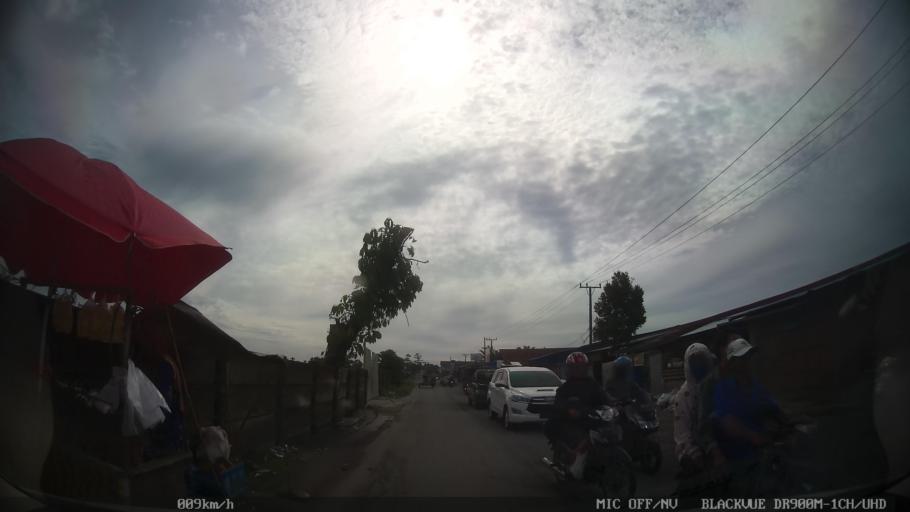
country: ID
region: North Sumatra
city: Medan
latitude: 3.6214
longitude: 98.7166
